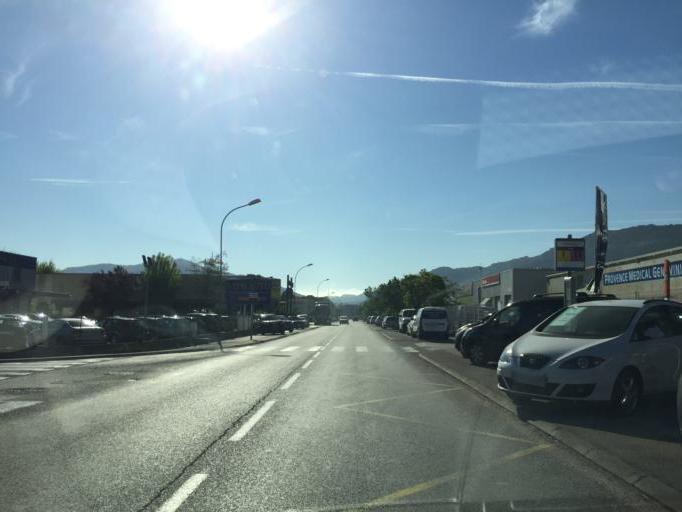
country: FR
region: Provence-Alpes-Cote d'Azur
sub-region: Departement des Bouches-du-Rhone
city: Aubagne
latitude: 43.2899
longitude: 5.5971
